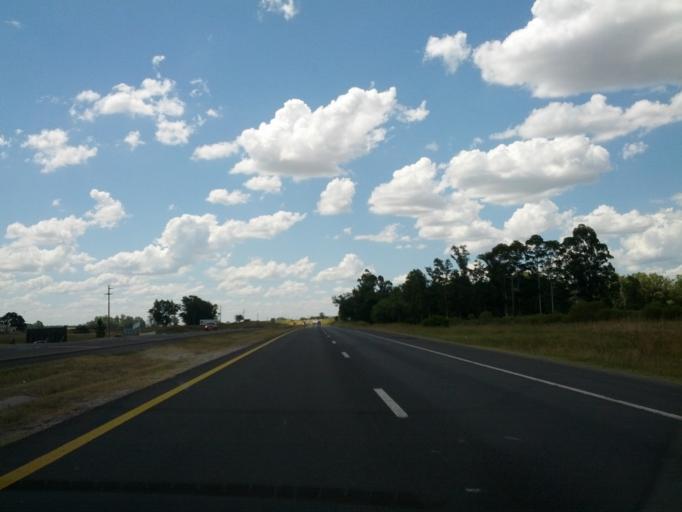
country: AR
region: Entre Rios
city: Concepcion del Uruguay
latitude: -32.3893
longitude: -58.2785
